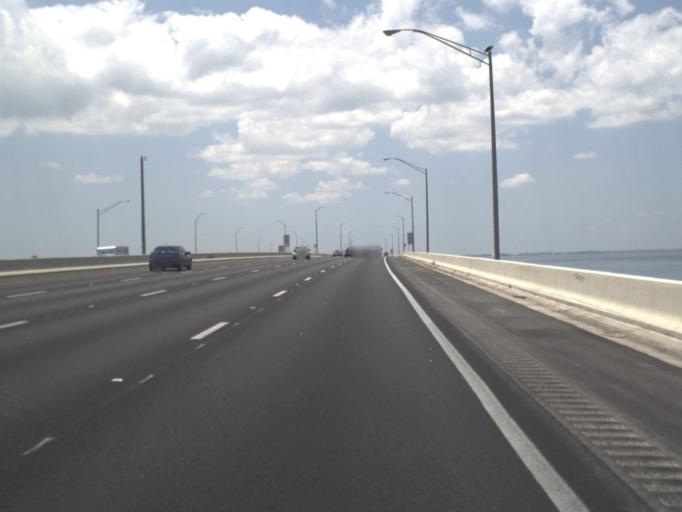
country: US
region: Florida
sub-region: Hillsborough County
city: Town 'n' Country
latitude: 27.9370
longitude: -82.5621
